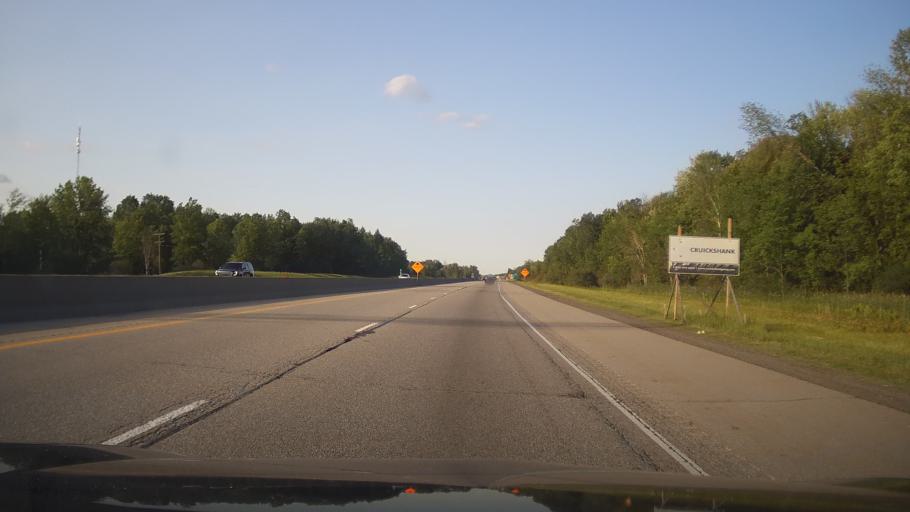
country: CA
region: Ontario
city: Brockville
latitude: 44.6409
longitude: -75.6426
